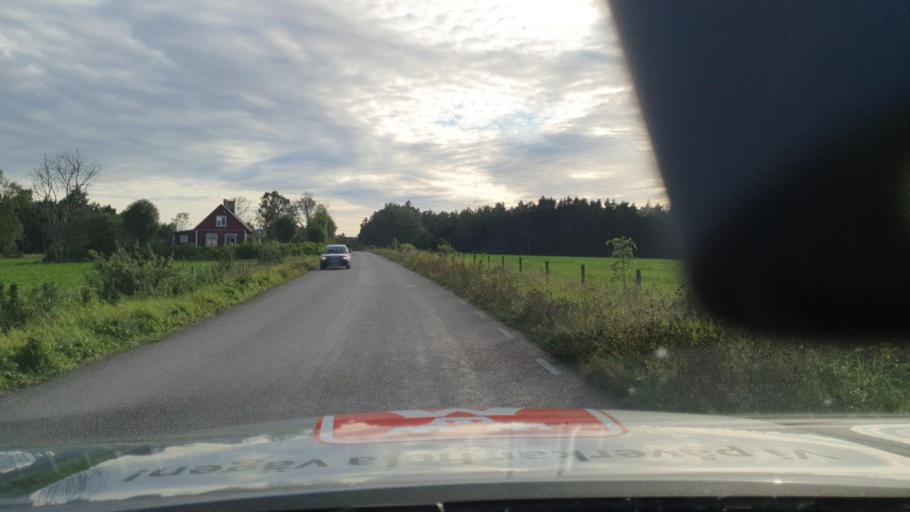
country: SE
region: Gotland
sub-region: Gotland
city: Hemse
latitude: 57.4059
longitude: 18.5467
